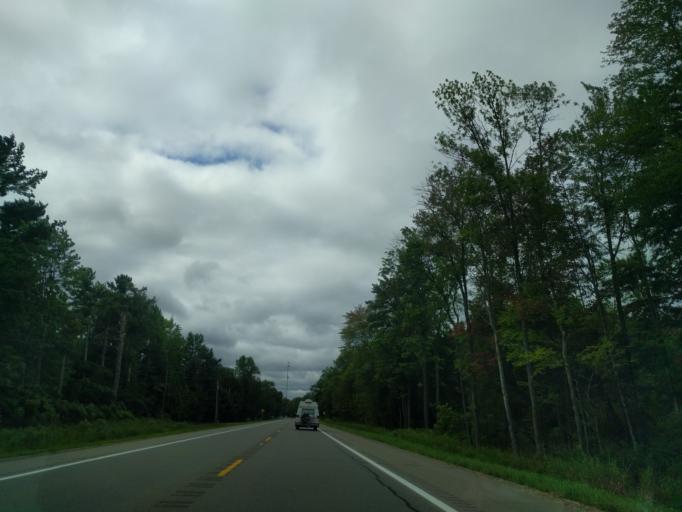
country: US
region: Michigan
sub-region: Menominee County
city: Menominee
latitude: 45.2765
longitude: -87.4638
